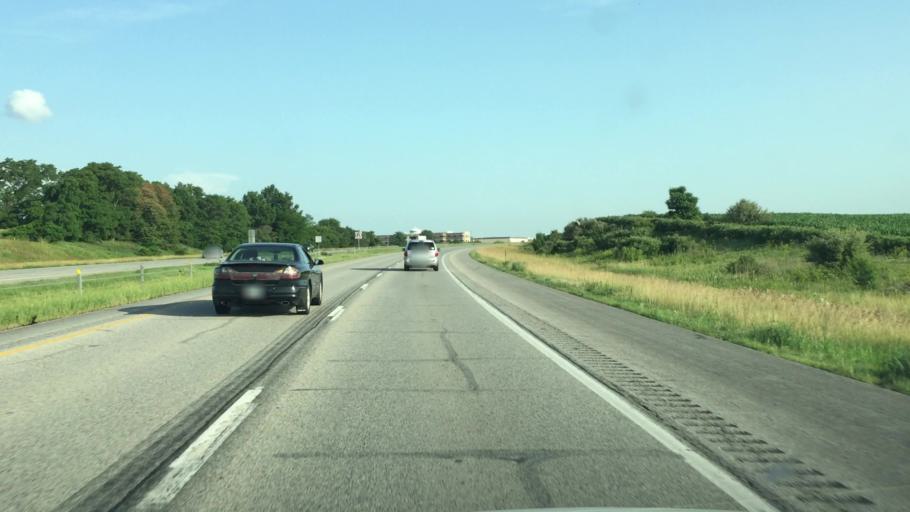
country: US
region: Iowa
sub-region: Johnson County
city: North Liberty
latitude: 41.7653
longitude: -91.6434
